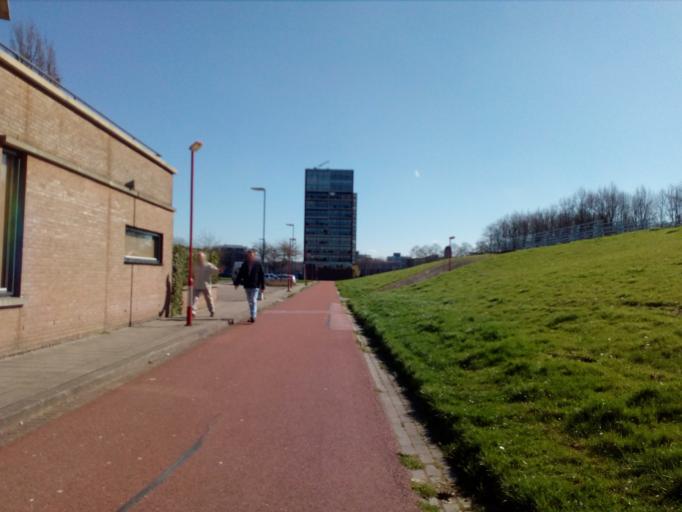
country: NL
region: South Holland
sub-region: Gemeente Zoetermeer
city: Zoetermeer
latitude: 52.0435
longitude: 4.4680
